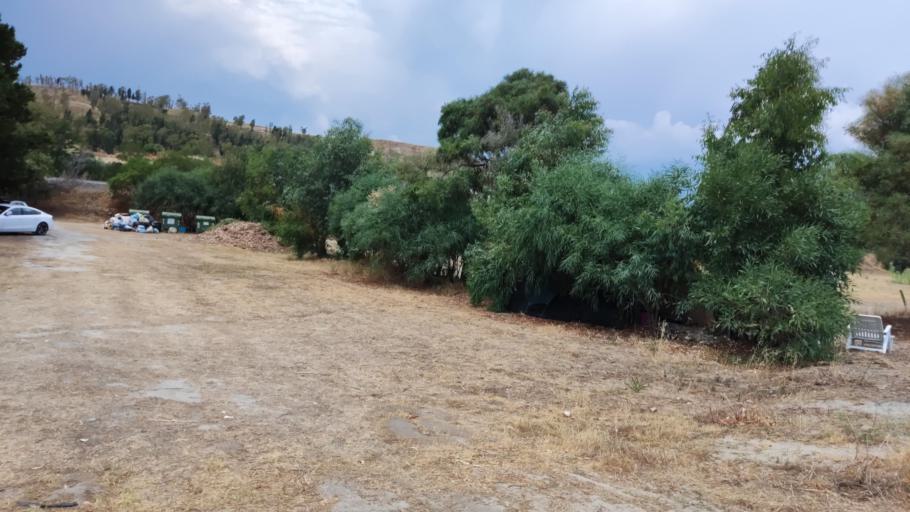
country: IT
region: Calabria
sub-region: Provincia di Catanzaro
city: Santa Caterina dello Ionio Marina
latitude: 38.5481
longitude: 16.5713
